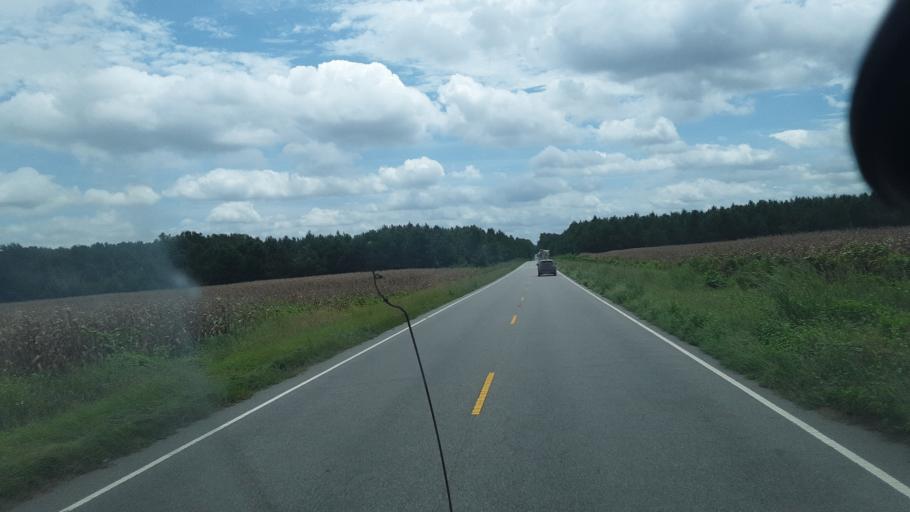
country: US
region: North Carolina
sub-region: Robeson County
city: Rowland
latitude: 34.4893
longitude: -79.2484
